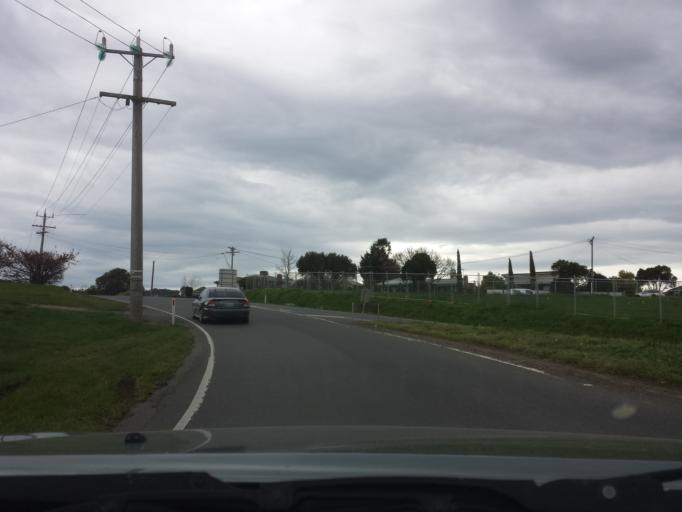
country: AU
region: Victoria
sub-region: Yarra Ranges
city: Yarra Glen
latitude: -37.6524
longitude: 145.3760
